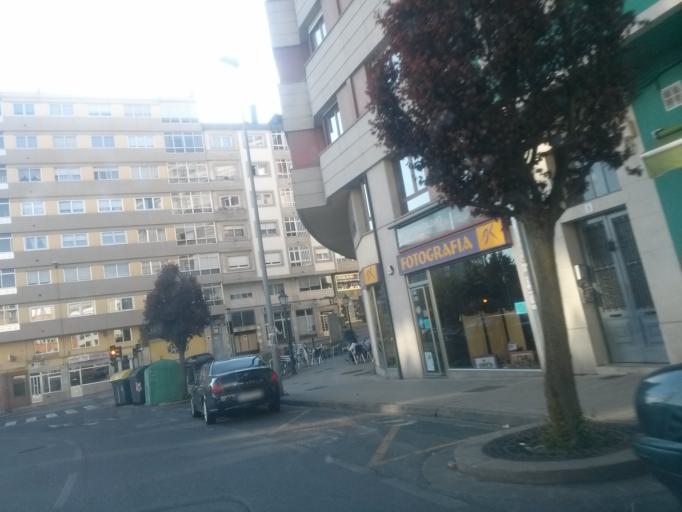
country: ES
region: Galicia
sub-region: Provincia de Lugo
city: Lugo
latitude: 43.0129
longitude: -7.5654
